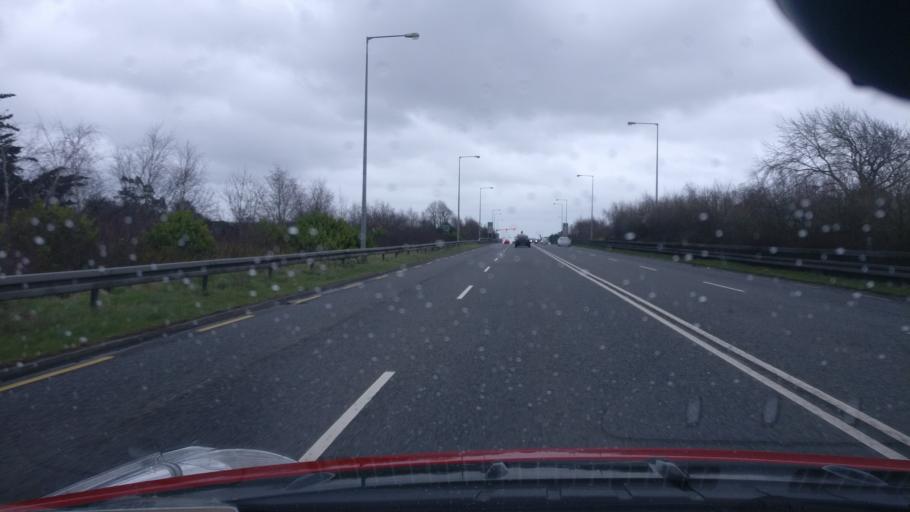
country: IE
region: Munster
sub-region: County Limerick
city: Annacotty
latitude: 52.6489
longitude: -8.5691
